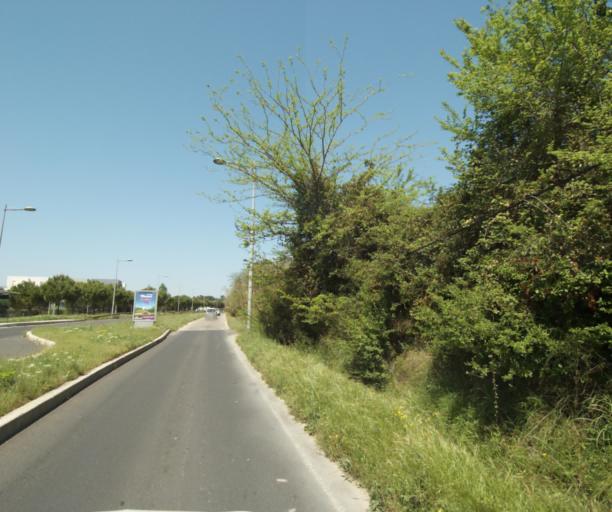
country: FR
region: Languedoc-Roussillon
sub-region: Departement de l'Herault
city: Juvignac
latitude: 43.6349
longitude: 3.8335
